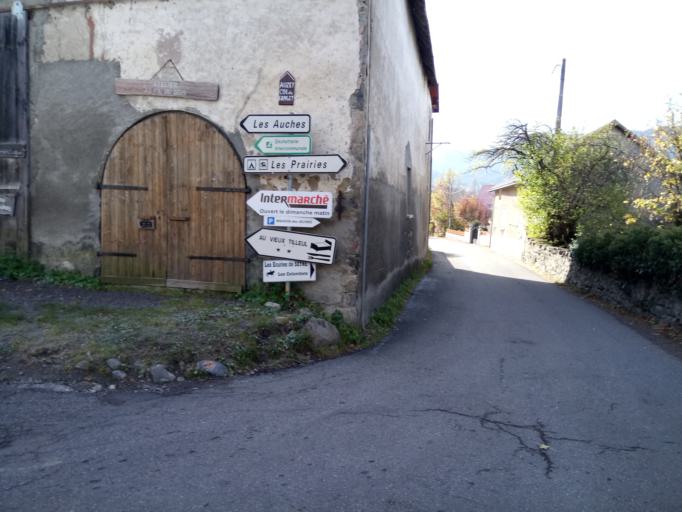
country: FR
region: Provence-Alpes-Cote d'Azur
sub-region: Departement des Alpes-de-Haute-Provence
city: Seyne-les-Alpes
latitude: 44.3484
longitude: 6.3592
